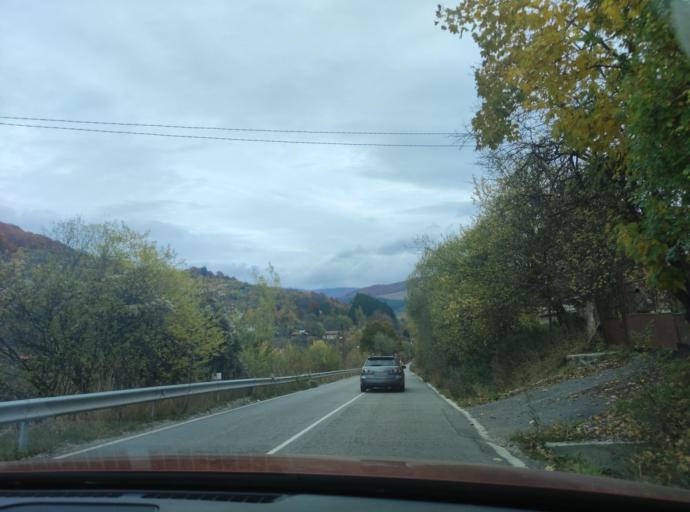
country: BG
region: Sofiya
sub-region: Obshtina Godech
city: Godech
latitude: 43.0672
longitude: 23.1079
